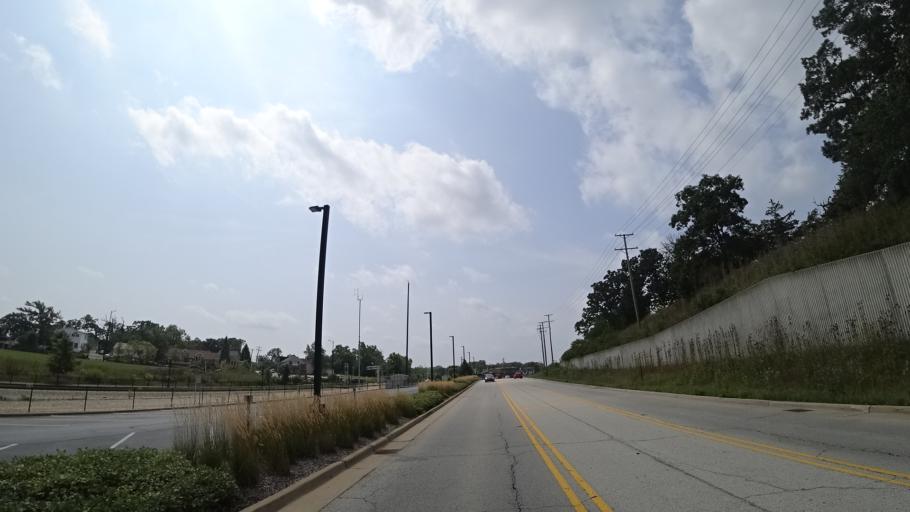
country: US
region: Illinois
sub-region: Cook County
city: Orland Park
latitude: 41.6315
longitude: -87.8590
